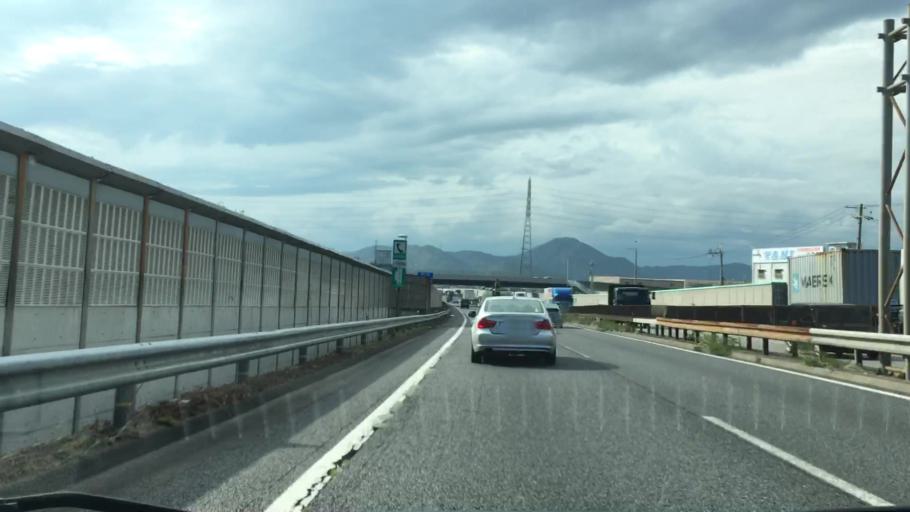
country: JP
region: Hyogo
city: Kakogawacho-honmachi
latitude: 34.7823
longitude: 134.8312
